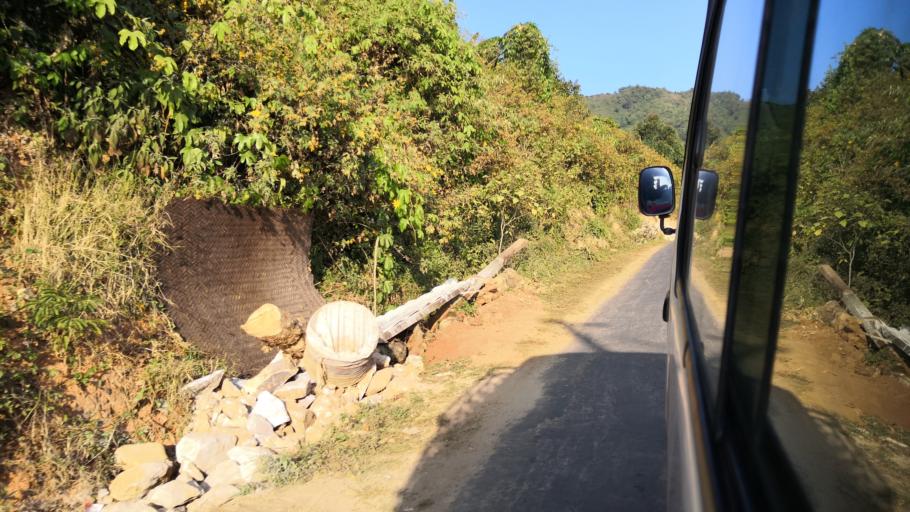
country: MM
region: Mandalay
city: Mogok
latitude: 22.9045
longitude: 96.3851
